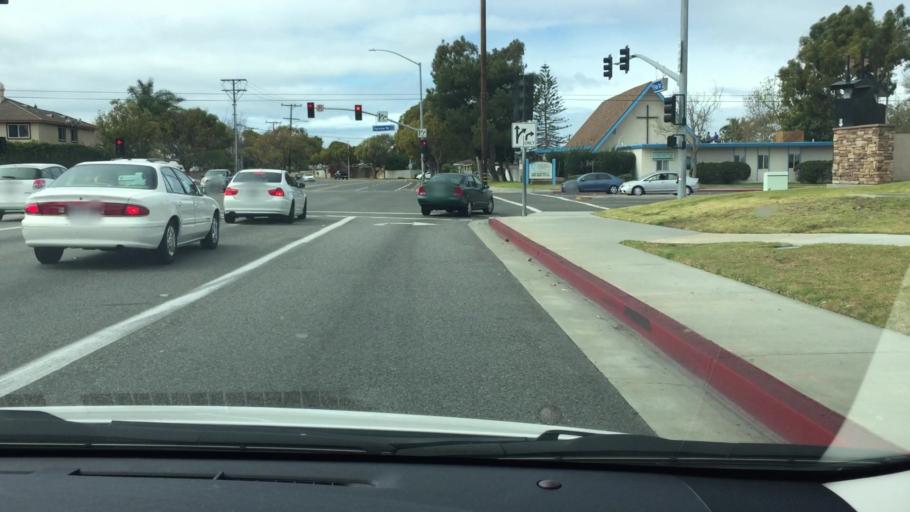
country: US
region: California
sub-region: Orange County
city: Costa Mesa
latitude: 33.6640
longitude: -117.9071
